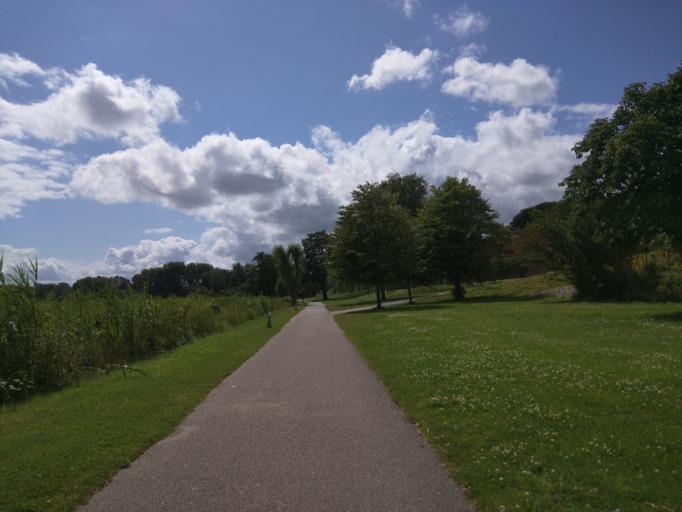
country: DK
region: Central Jutland
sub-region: Viborg Kommune
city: Viborg
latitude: 56.4426
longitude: 9.4056
